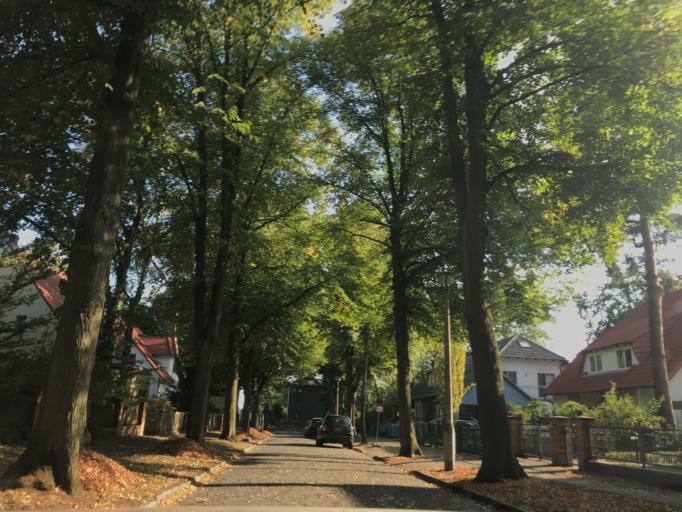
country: DE
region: Brandenburg
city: Kleinmachnow
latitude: 52.4073
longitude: 13.2424
